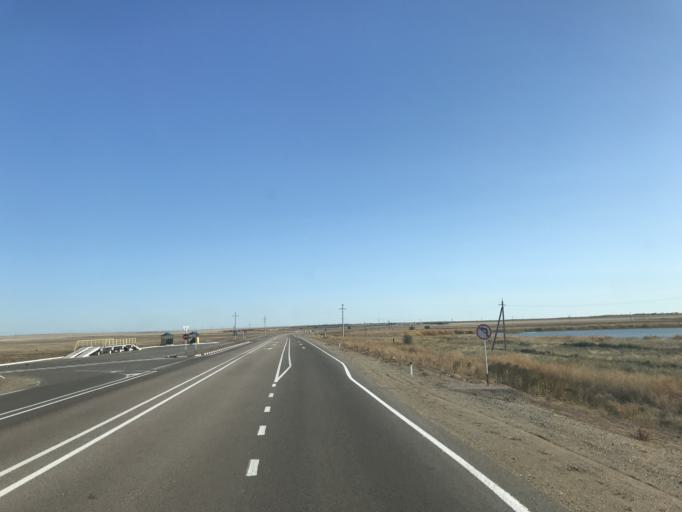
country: KZ
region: Pavlodar
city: Koktobe
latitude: 51.8833
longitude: 77.4172
